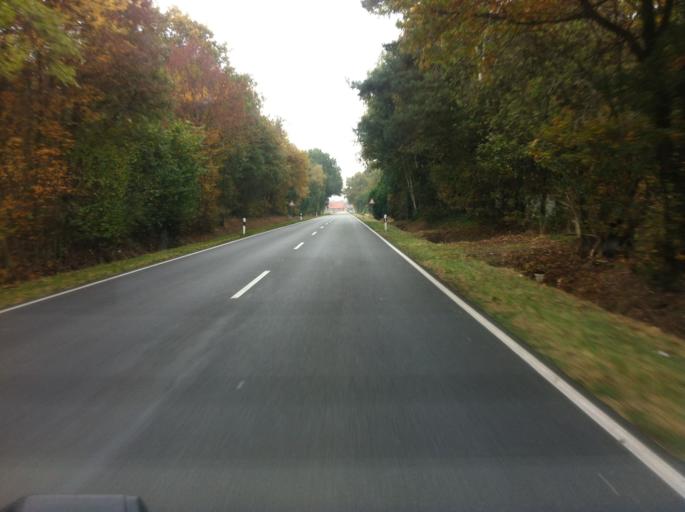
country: DE
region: North Rhine-Westphalia
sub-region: Regierungsbezirk Munster
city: Vreden
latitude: 52.1033
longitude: 6.8895
